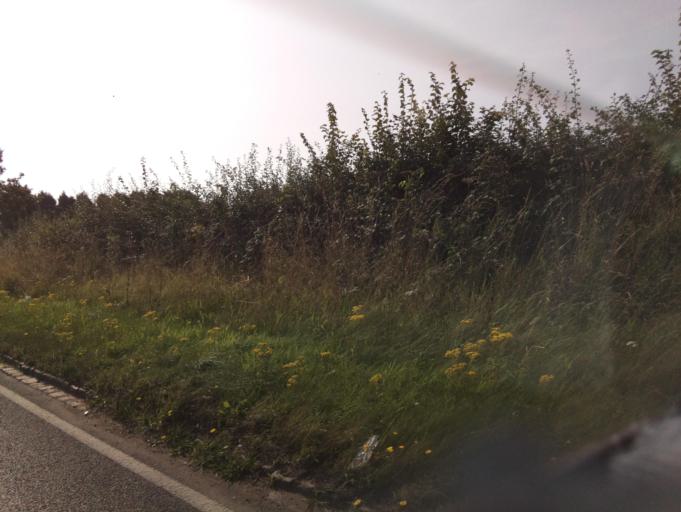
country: GB
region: England
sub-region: Walsall
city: Aldridge
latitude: 52.6245
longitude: -1.8971
